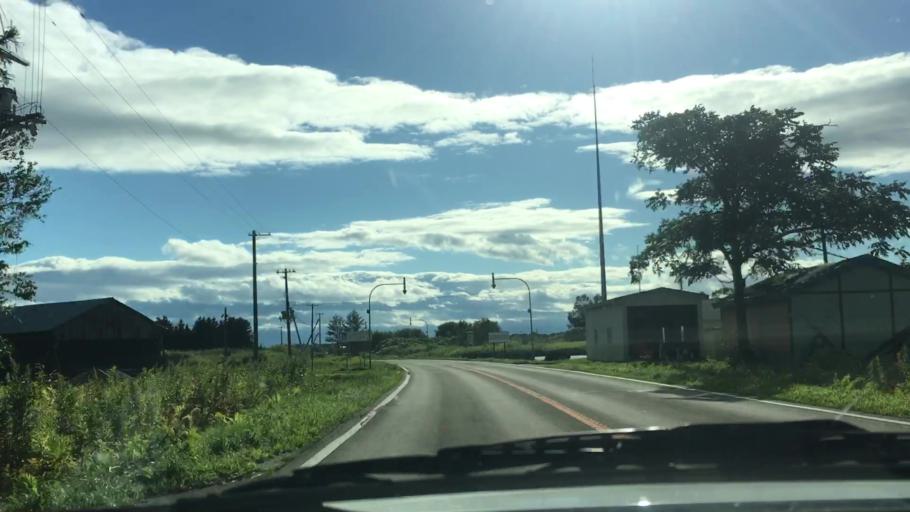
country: JP
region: Hokkaido
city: Otofuke
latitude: 43.1620
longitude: 143.2502
